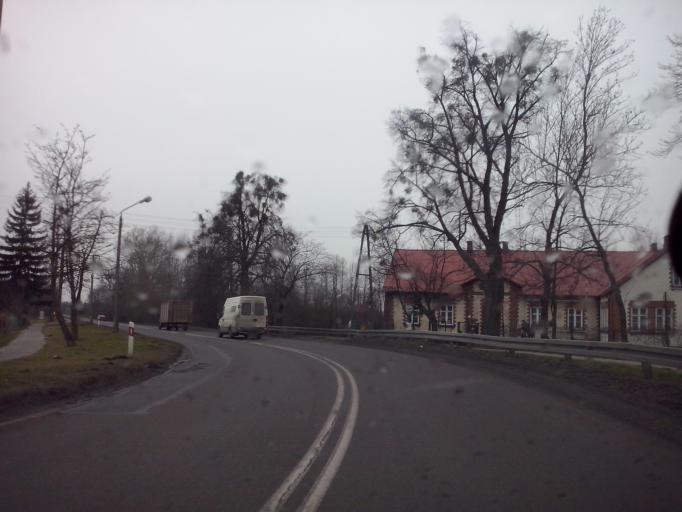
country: PL
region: Lublin Voivodeship
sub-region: Powiat zamojski
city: Michalow
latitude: 50.7134
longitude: 23.0081
